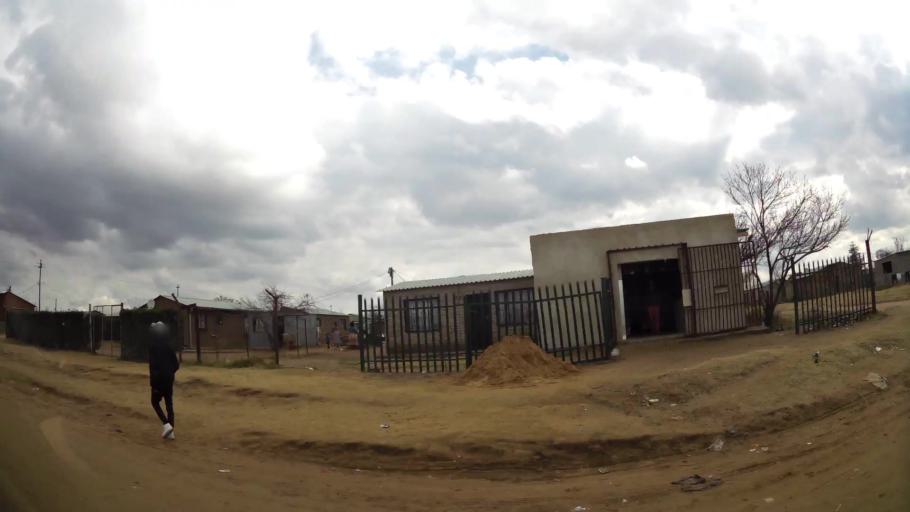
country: ZA
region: Orange Free State
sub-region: Fezile Dabi District Municipality
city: Sasolburg
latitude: -26.8666
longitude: 27.8709
